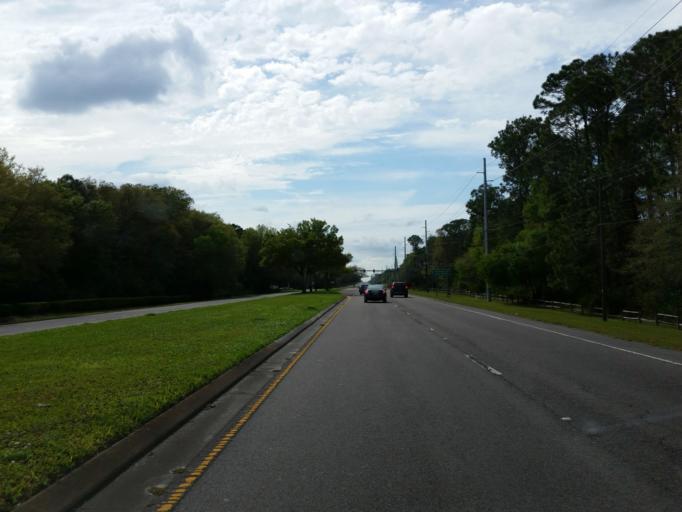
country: US
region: Florida
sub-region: Hillsborough County
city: Temple Terrace
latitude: 28.0693
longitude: -82.3714
